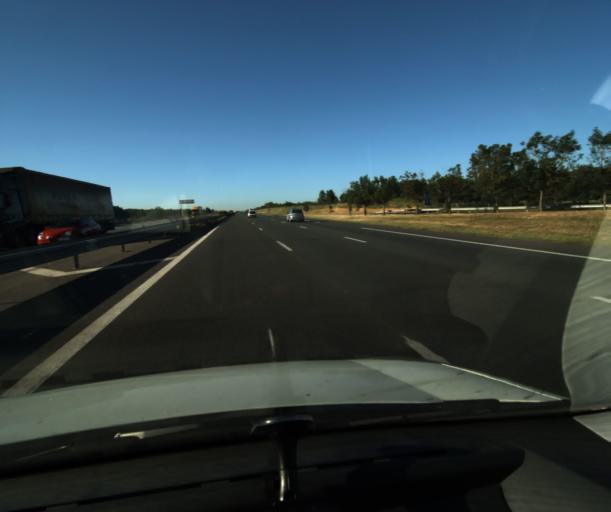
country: FR
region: Midi-Pyrenees
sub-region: Departement du Tarn-et-Garonne
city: Campsas
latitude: 43.8862
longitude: 1.3172
